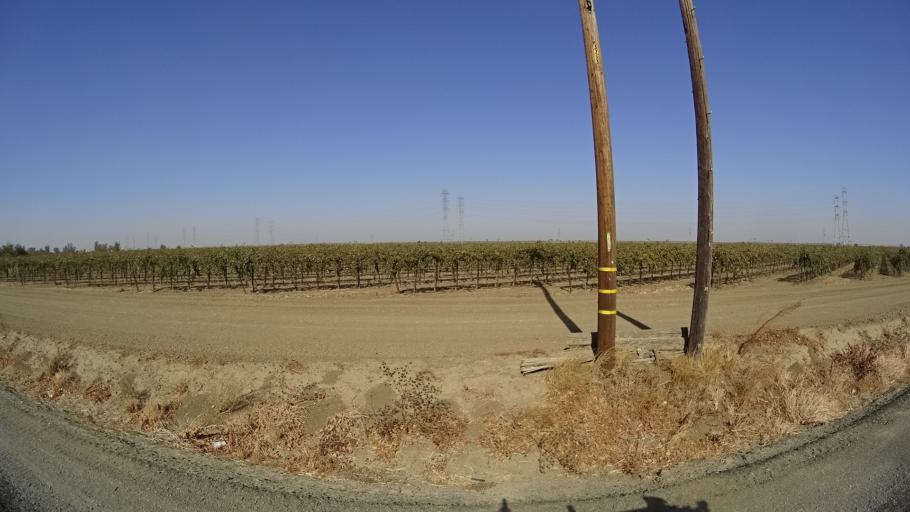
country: US
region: California
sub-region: Yolo County
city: Esparto
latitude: 38.7285
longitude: -121.9779
